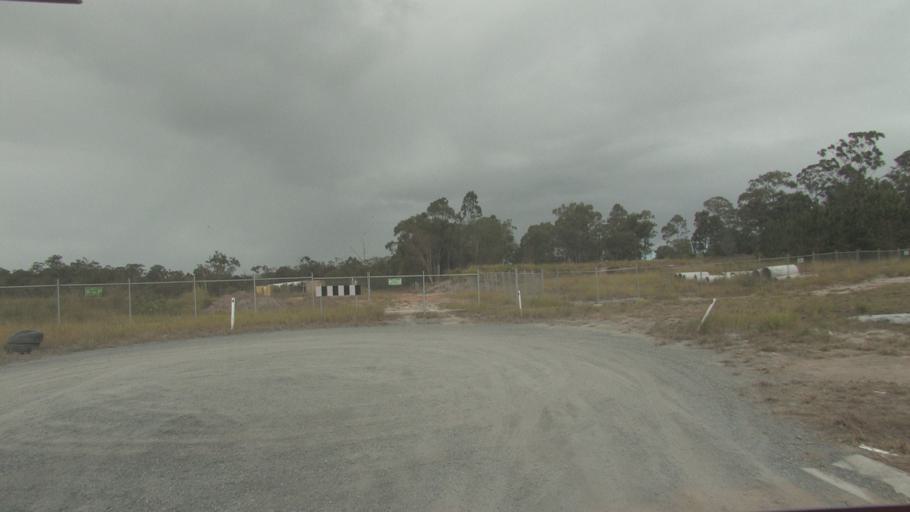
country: AU
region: Queensland
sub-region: Logan
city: Park Ridge South
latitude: -27.6923
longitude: 153.0481
